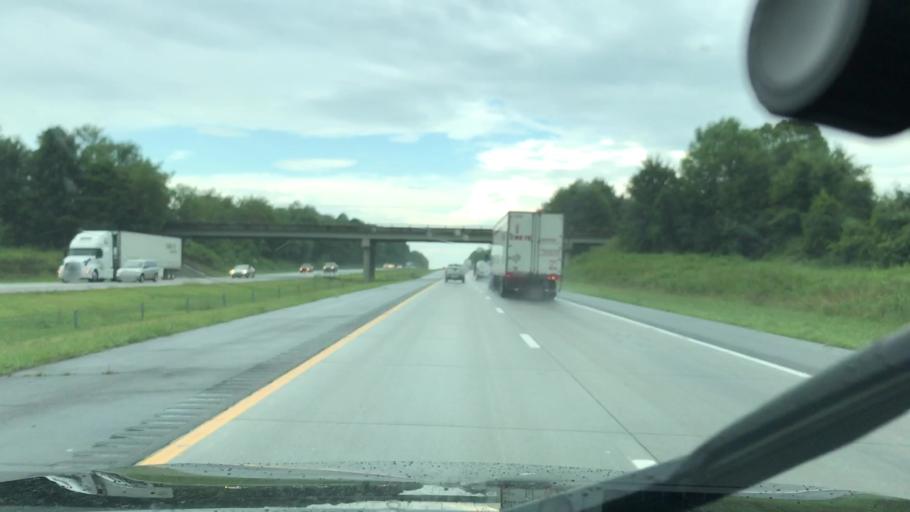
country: US
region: North Carolina
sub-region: Yadkin County
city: Jonesville
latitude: 36.1559
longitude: -80.8078
